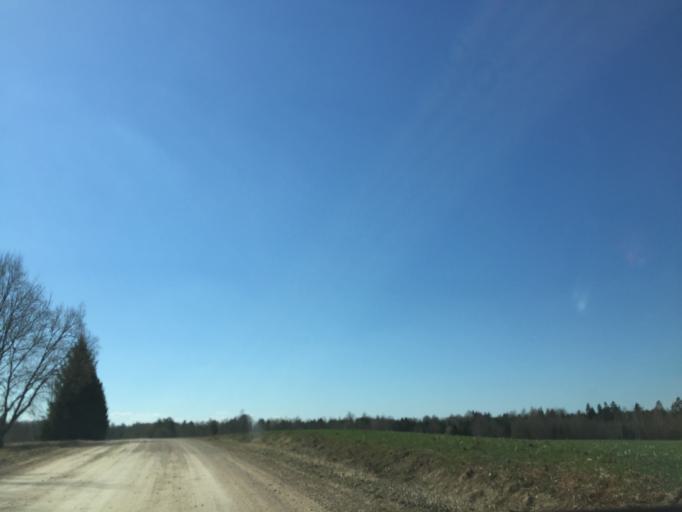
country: EE
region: Viljandimaa
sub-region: Viiratsi vald
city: Viiratsi
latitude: 58.3154
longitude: 25.6905
